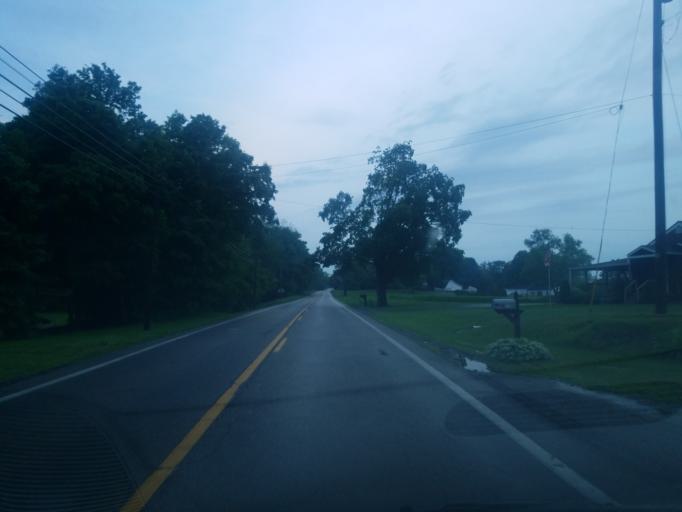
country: US
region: Ohio
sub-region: Columbiana County
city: Salem
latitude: 40.8835
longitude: -80.8767
